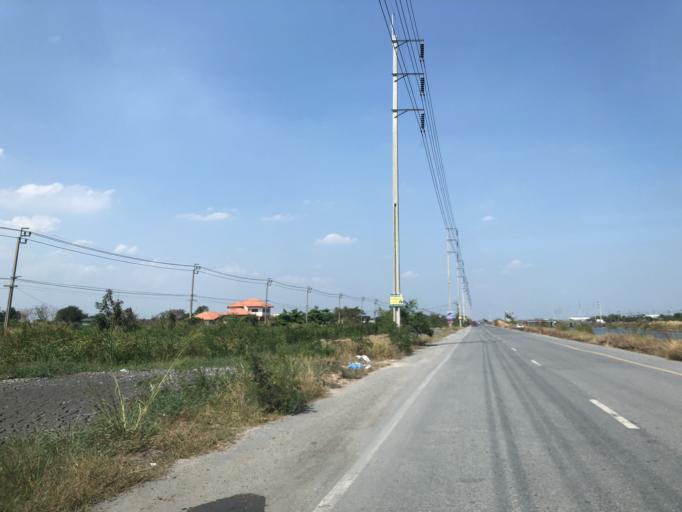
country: TH
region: Samut Prakan
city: Bang Bo District
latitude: 13.5223
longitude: 100.7472
